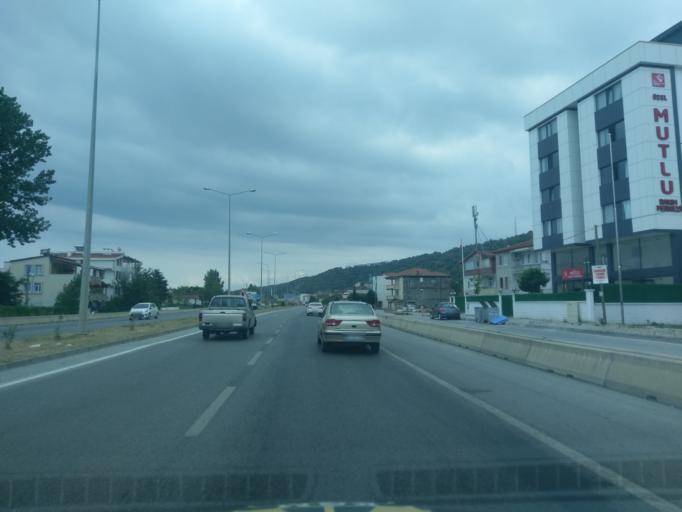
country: TR
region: Samsun
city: Taflan
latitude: 41.3932
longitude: 36.2002
